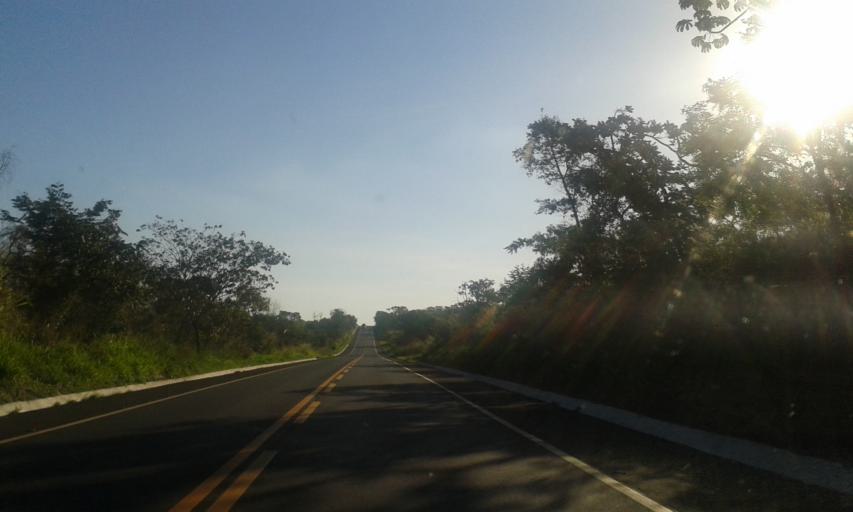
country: BR
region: Minas Gerais
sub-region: Ituiutaba
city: Ituiutaba
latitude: -18.8805
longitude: -49.1862
